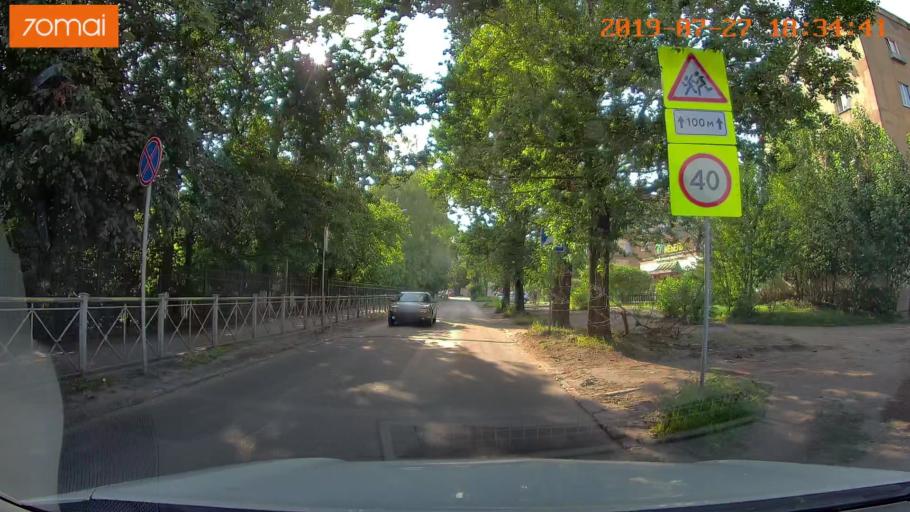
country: RU
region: Kaliningrad
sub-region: Gorod Kaliningrad
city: Kaliningrad
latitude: 54.7028
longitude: 20.5025
